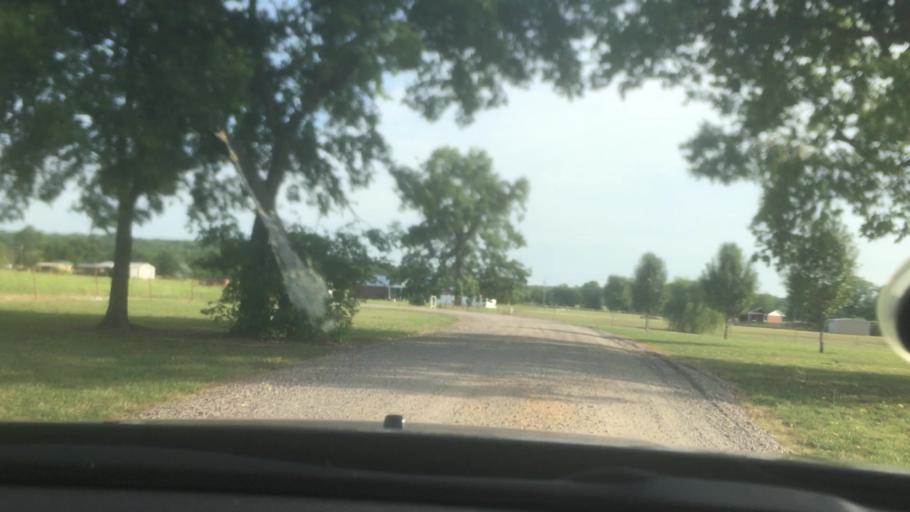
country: US
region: Oklahoma
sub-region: Pontotoc County
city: Ada
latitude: 34.7213
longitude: -96.6677
